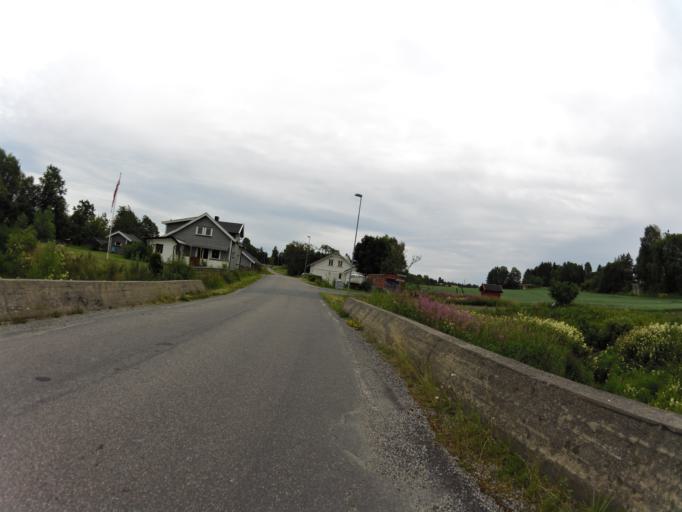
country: NO
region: Akershus
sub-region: Vestby
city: Vestby
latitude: 59.5330
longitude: 10.7457
